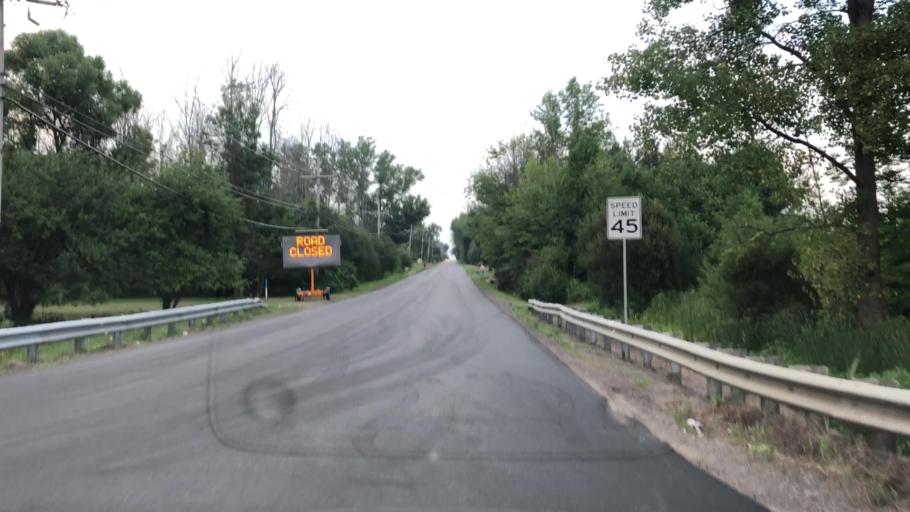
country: US
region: New York
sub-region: Erie County
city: Billington Heights
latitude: 42.8052
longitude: -78.6059
